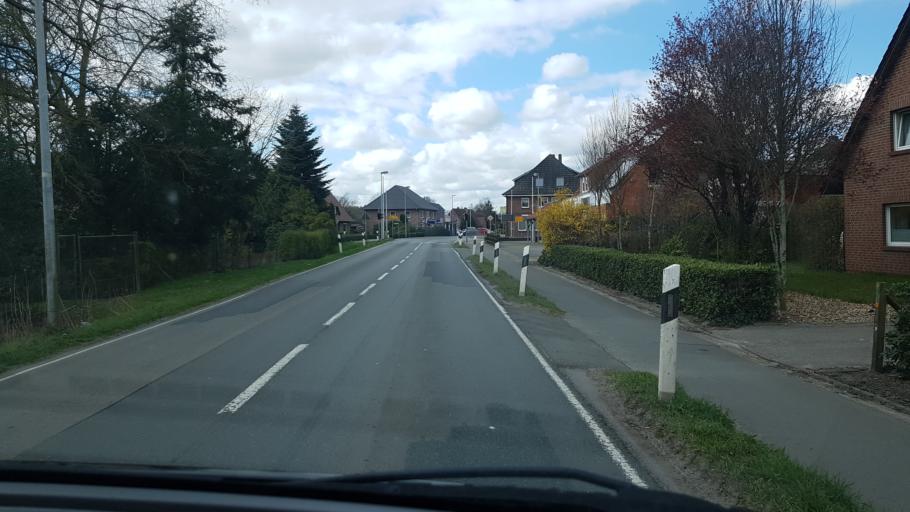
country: DE
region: Lower Saxony
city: Edewecht
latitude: 53.1219
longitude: 7.9316
